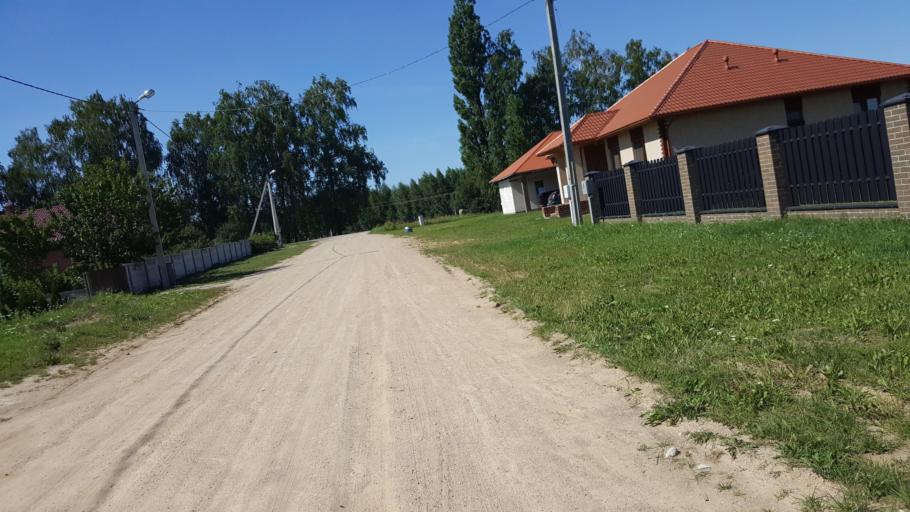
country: BY
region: Brest
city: Charnawchytsy
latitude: 52.2598
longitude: 23.5902
